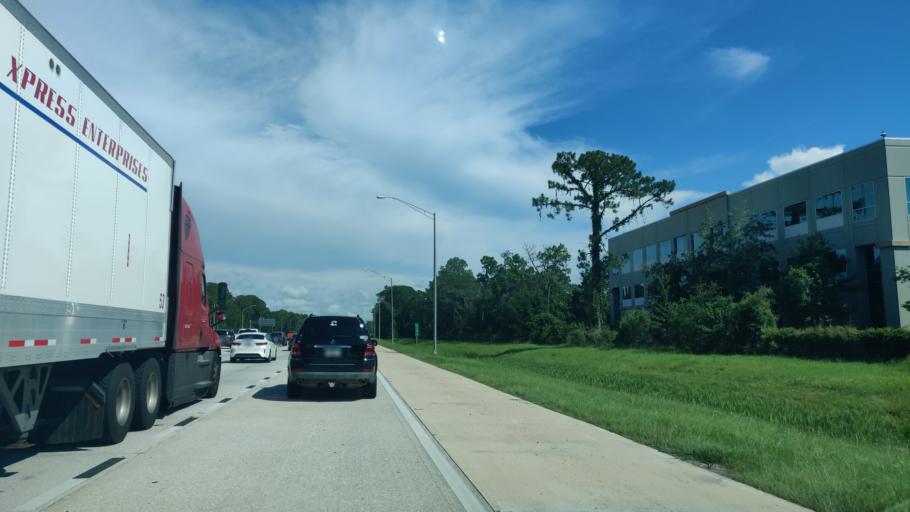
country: US
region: Florida
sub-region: Duval County
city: Jacksonville
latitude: 30.2427
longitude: -81.5876
